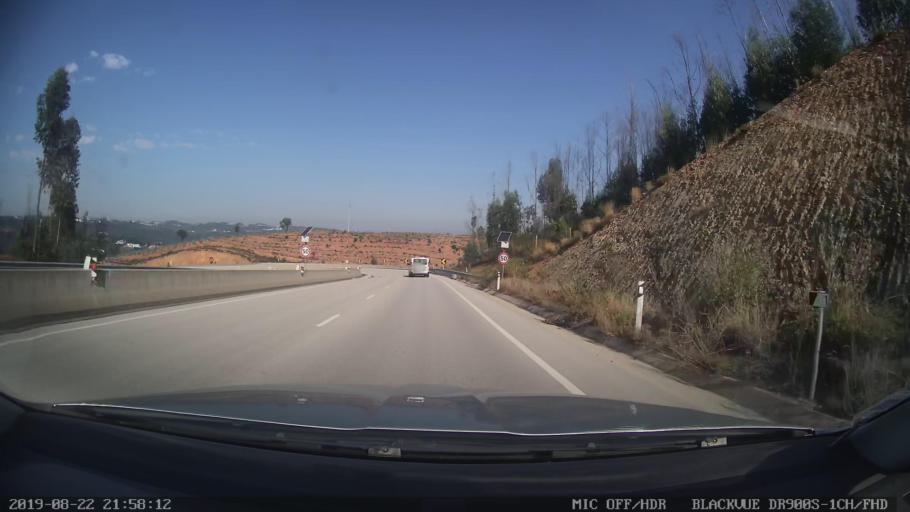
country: PT
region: Coimbra
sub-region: Coimbra
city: Coimbra
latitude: 40.1782
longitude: -8.3859
